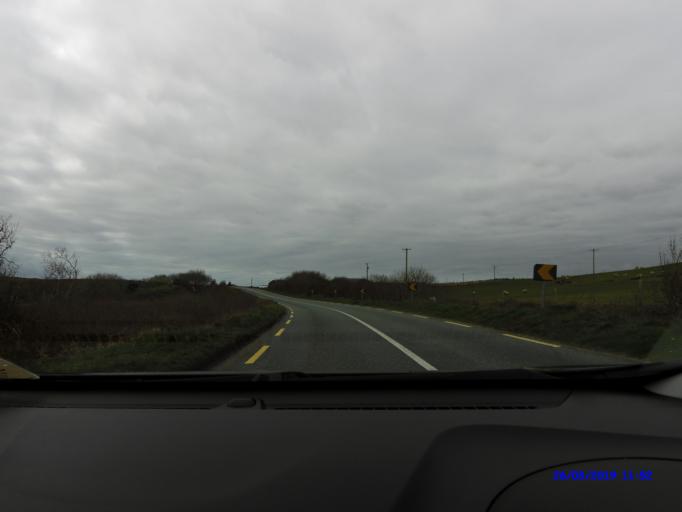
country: IE
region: Connaught
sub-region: Maigh Eo
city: Belmullet
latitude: 54.1754
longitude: -9.8423
